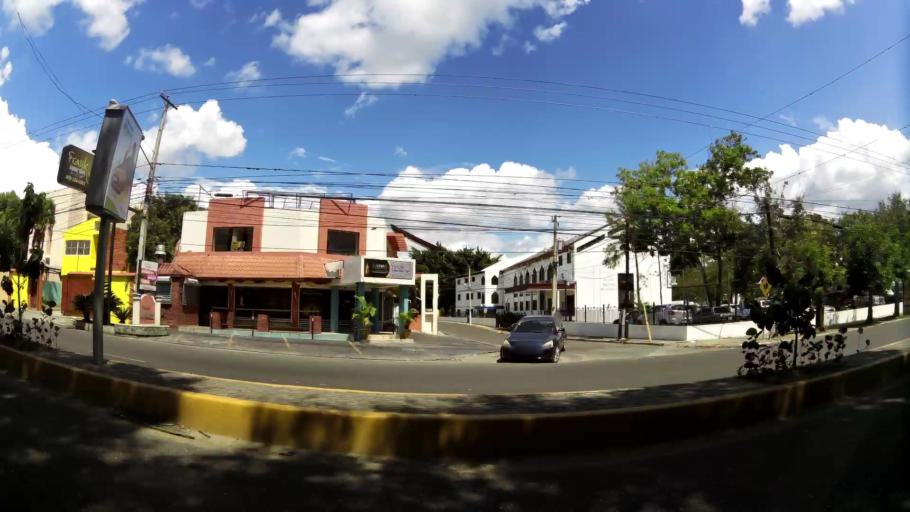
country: DO
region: Santiago
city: Santiago de los Caballeros
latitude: 19.4453
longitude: -70.6878
